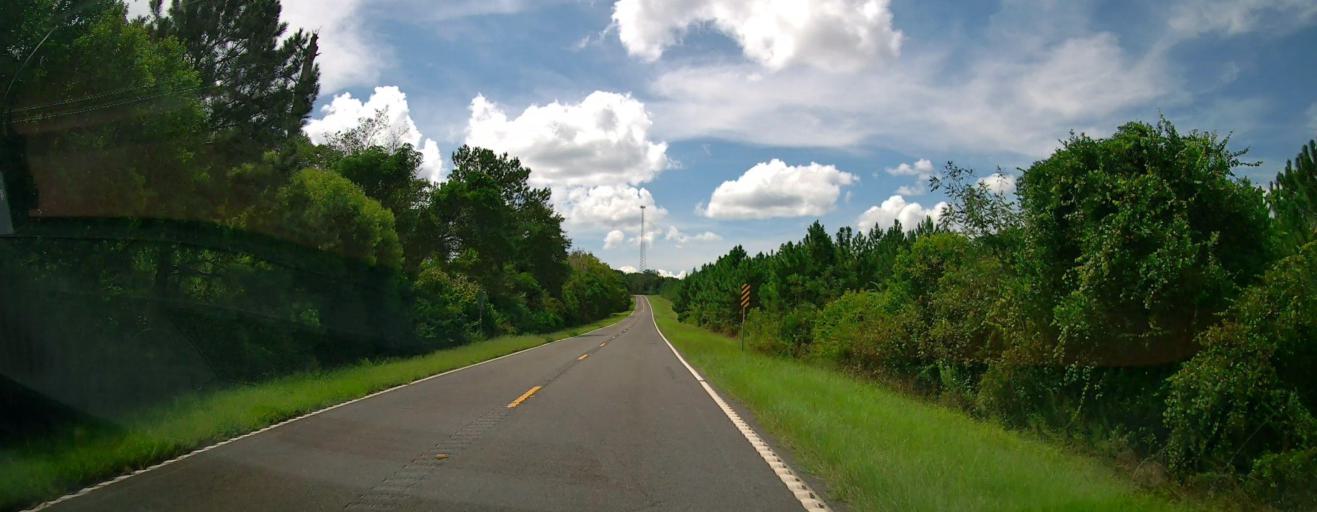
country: US
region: Georgia
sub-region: Taylor County
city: Reynolds
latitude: 32.4373
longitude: -84.1536
